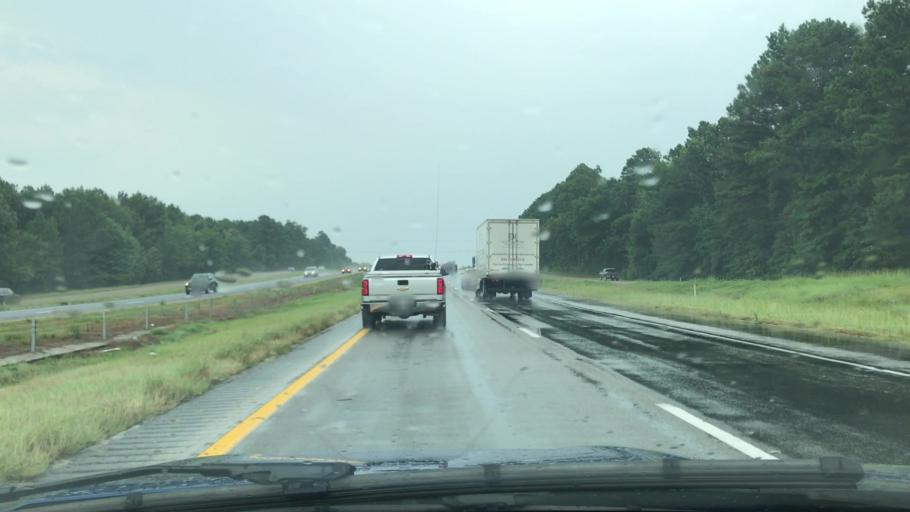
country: US
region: Texas
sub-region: Harrison County
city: Waskom
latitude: 32.4909
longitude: -94.1494
